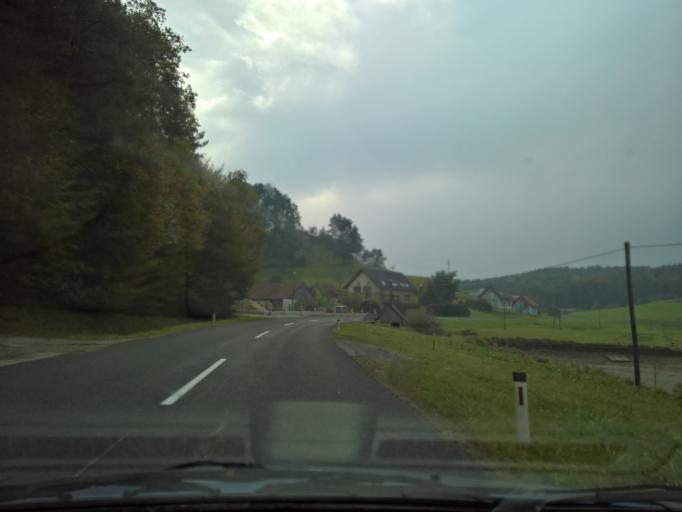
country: AT
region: Styria
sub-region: Politischer Bezirk Leibnitz
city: Pistorf
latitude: 46.7805
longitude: 15.3402
